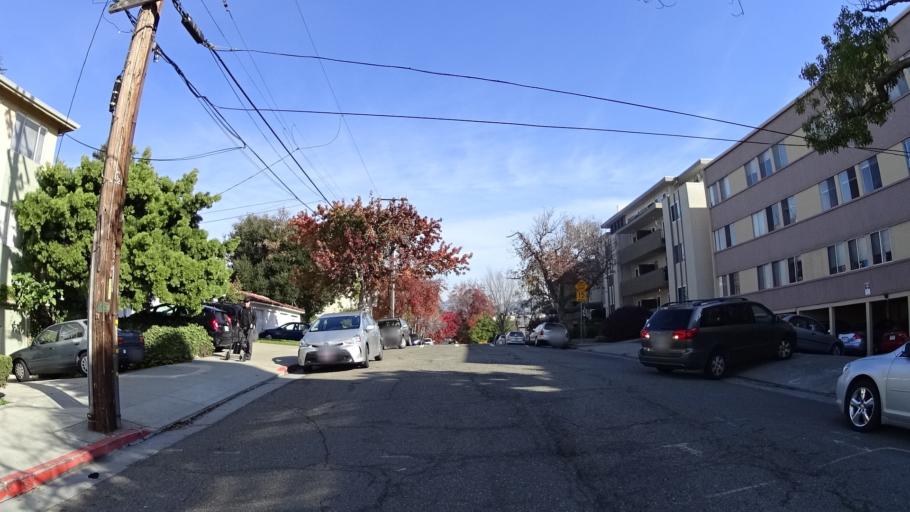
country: US
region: California
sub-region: Alameda County
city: Oakland
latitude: 37.8157
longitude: -122.2554
